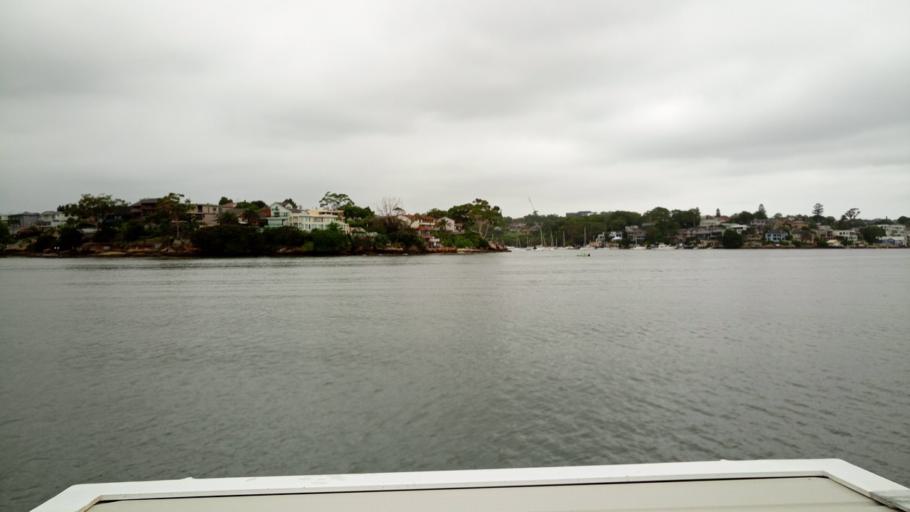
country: AU
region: New South Wales
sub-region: Canada Bay
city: Concord
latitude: -33.8388
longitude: 151.1135
